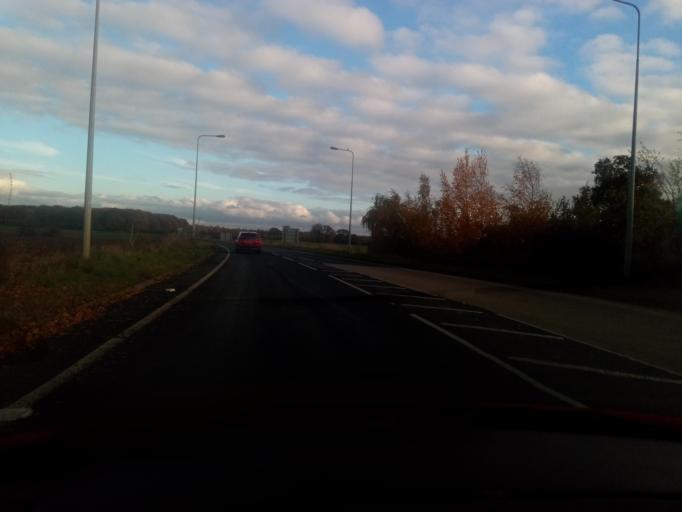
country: GB
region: England
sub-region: City and Borough of Leeds
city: Wetherby
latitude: 53.9451
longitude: -1.3871
